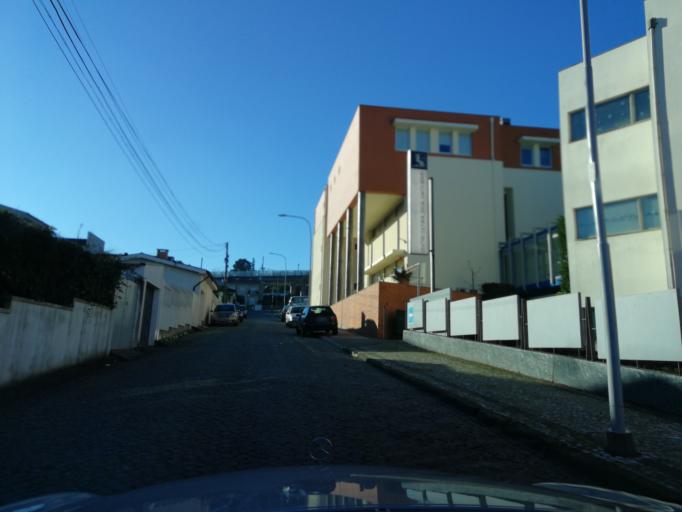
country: PT
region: Braga
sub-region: Braga
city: Braga
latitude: 41.5377
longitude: -8.4099
